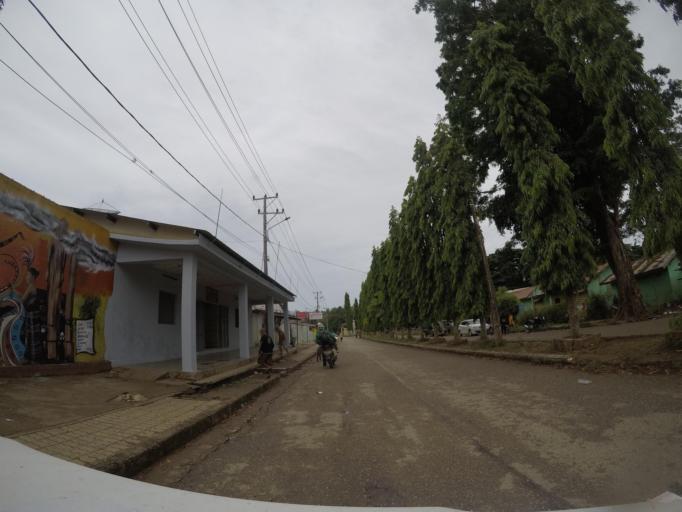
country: TL
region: Lautem
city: Lospalos
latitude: -8.5238
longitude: 126.9968
